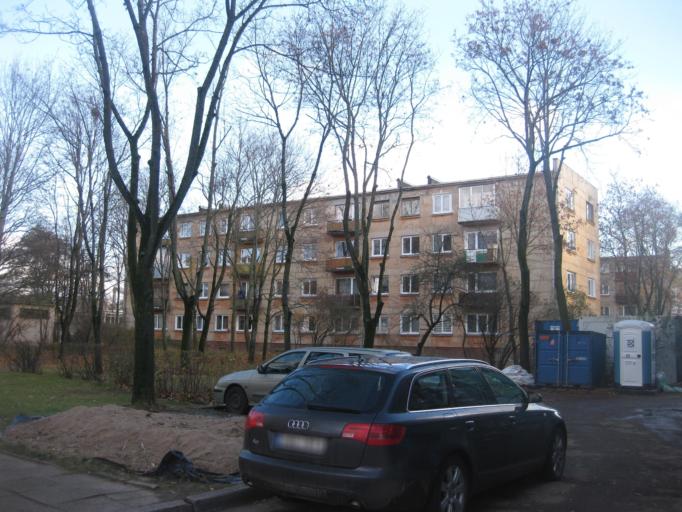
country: LT
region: Kauno apskritis
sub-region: Kaunas
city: Kaunas
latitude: 54.9118
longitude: 23.8911
